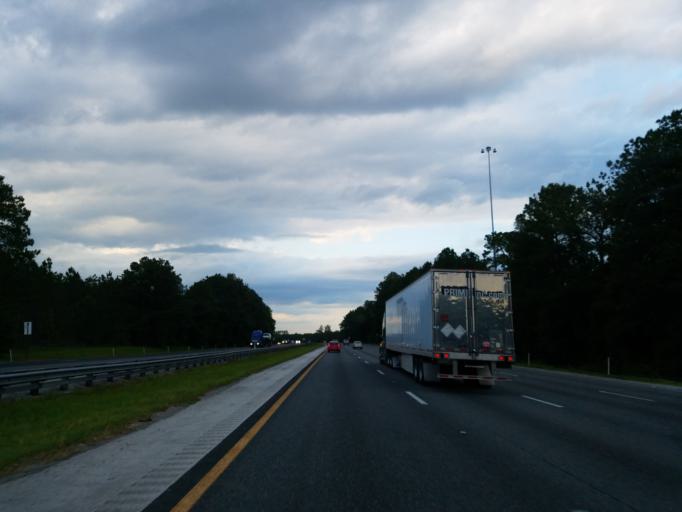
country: US
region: Florida
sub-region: Alachua County
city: High Springs
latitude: 29.8053
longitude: -82.5134
